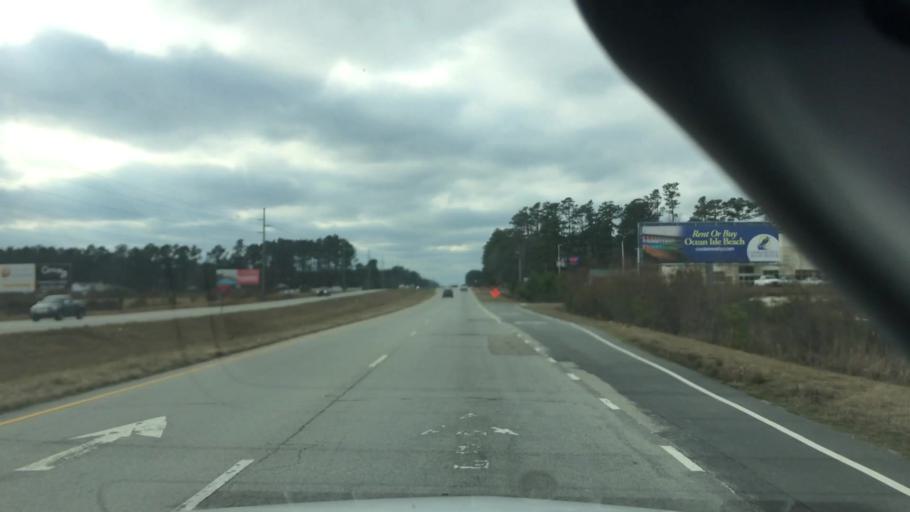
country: US
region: North Carolina
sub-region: Brunswick County
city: Shallotte
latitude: 33.9571
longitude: -78.4329
